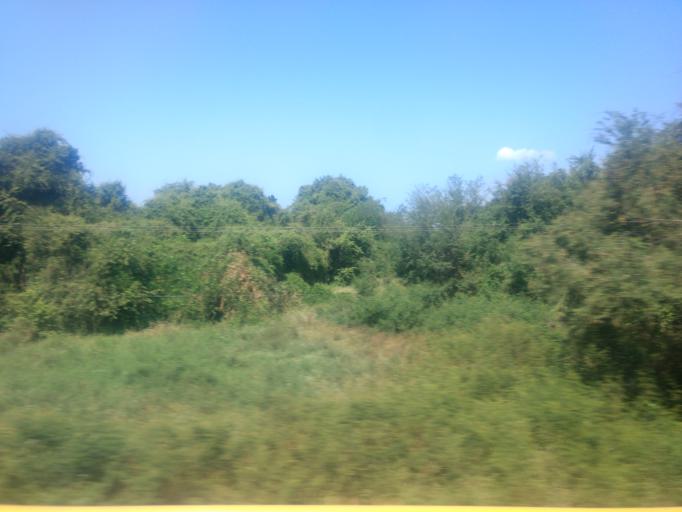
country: MX
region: Colima
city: El Colomo
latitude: 19.0429
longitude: -104.2600
